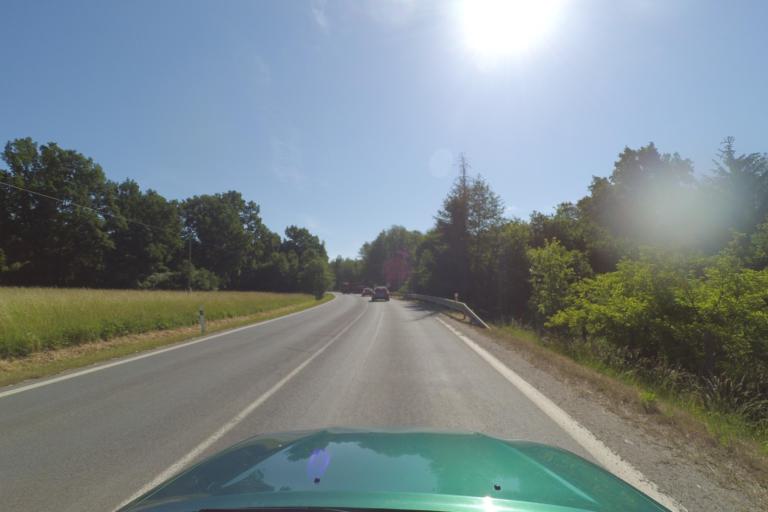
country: CZ
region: Karlovarsky
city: Chodov
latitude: 50.2396
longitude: 12.7763
